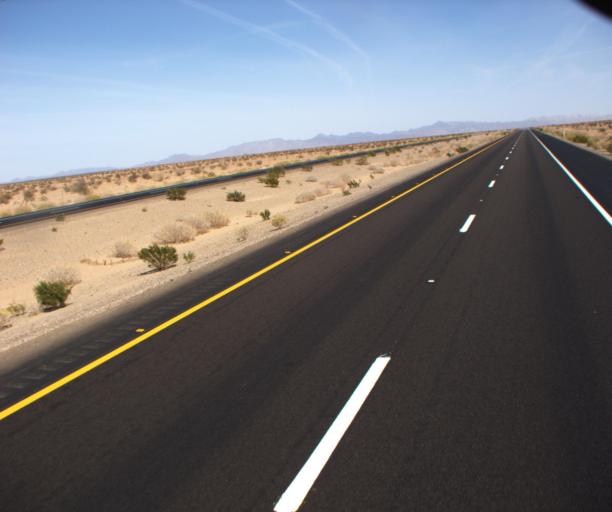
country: US
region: Arizona
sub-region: Yuma County
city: Somerton
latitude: 32.4951
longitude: -114.5947
